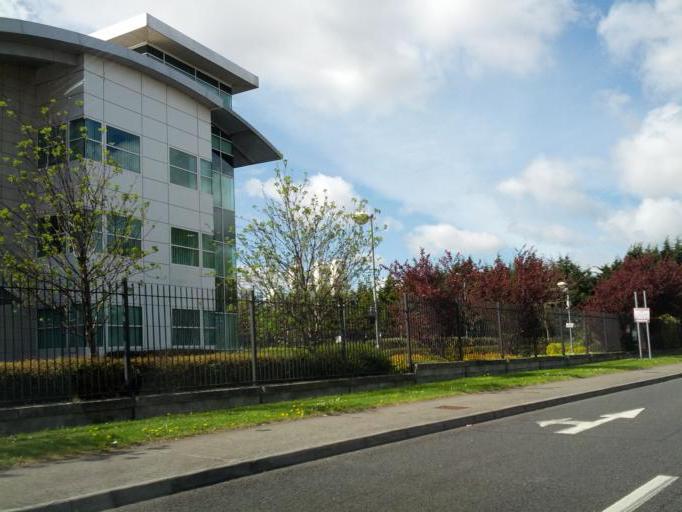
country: IE
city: Cherry Orchard
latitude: 53.3267
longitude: -6.3628
